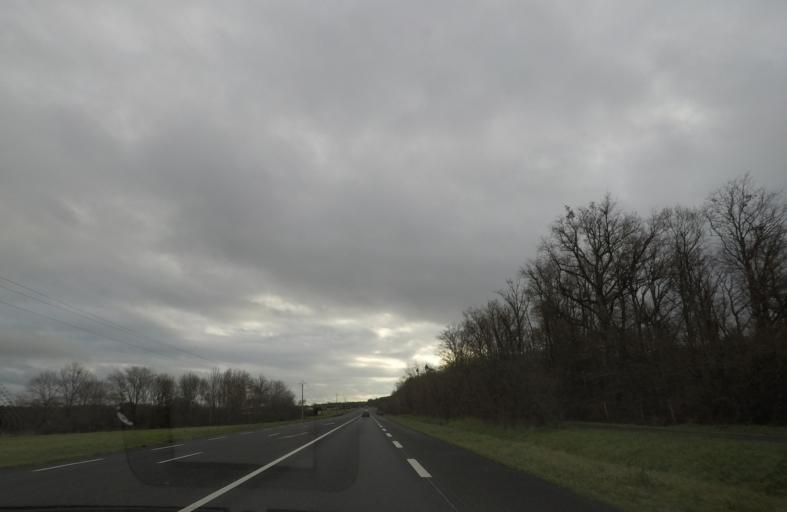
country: FR
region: Centre
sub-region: Departement du Loir-et-Cher
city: Soings-en-Sologne
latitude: 47.4457
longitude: 1.5405
